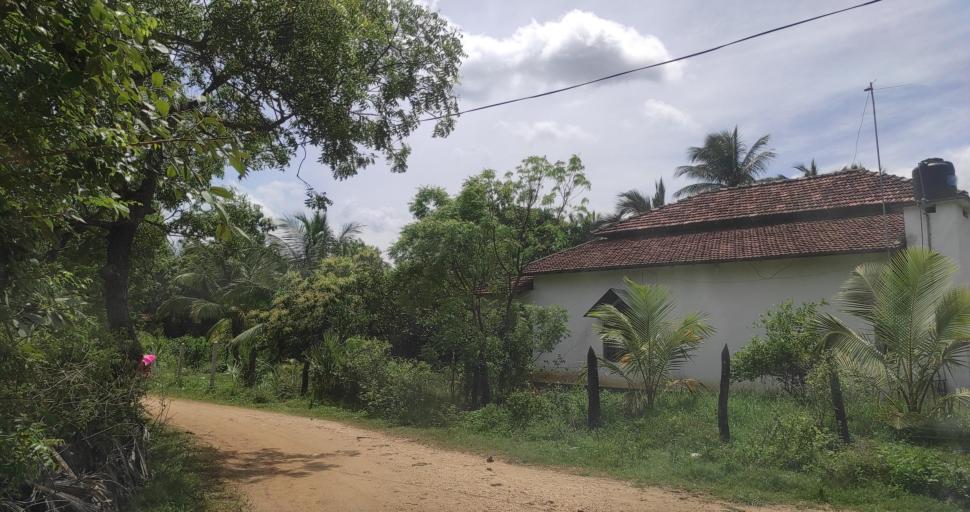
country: LK
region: Eastern Province
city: Trincomalee
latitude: 8.4418
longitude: 81.0490
